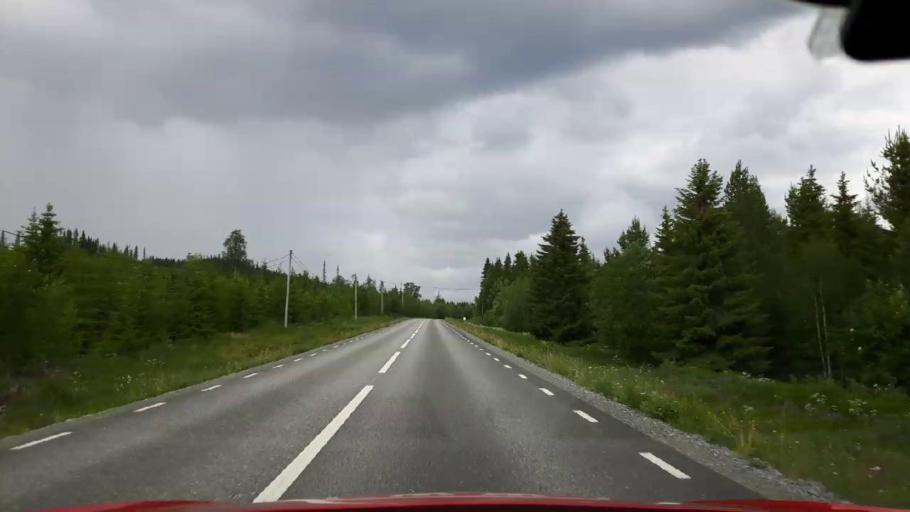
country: SE
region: Jaemtland
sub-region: Krokoms Kommun
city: Krokom
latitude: 63.6909
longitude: 14.3219
